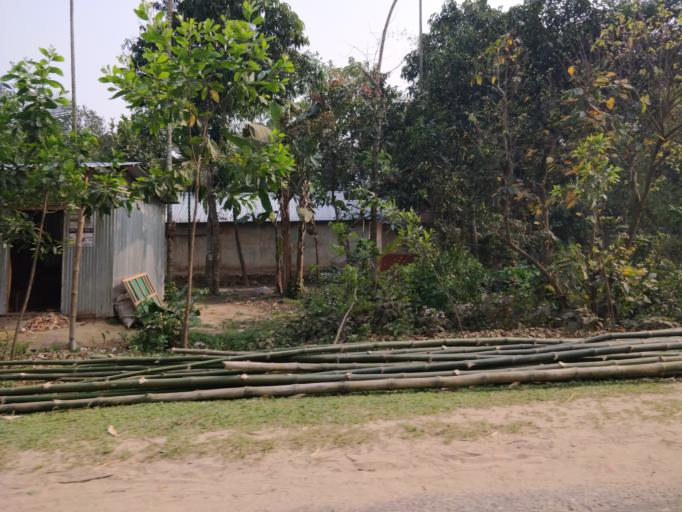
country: IN
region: Tripura
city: Khowai
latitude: 24.1296
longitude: 91.3754
